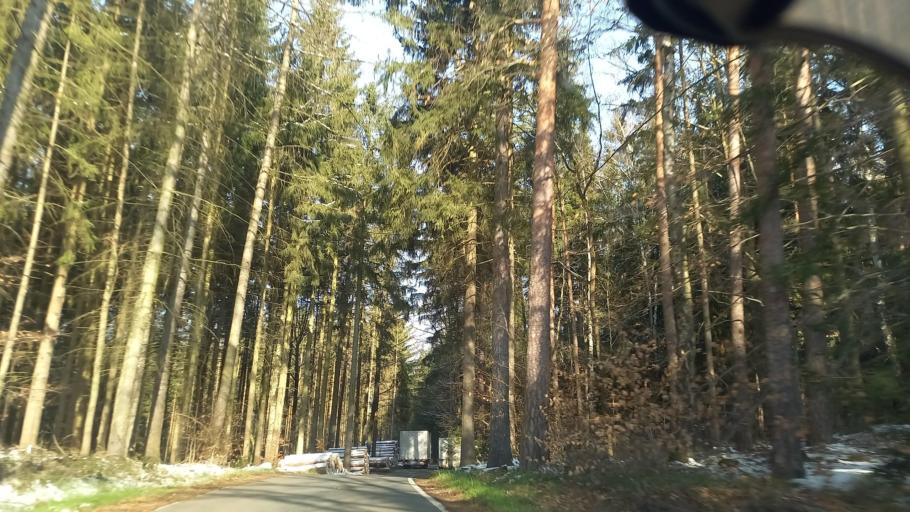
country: DE
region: Saxony
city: Kirchberg
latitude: 50.5844
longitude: 12.5052
